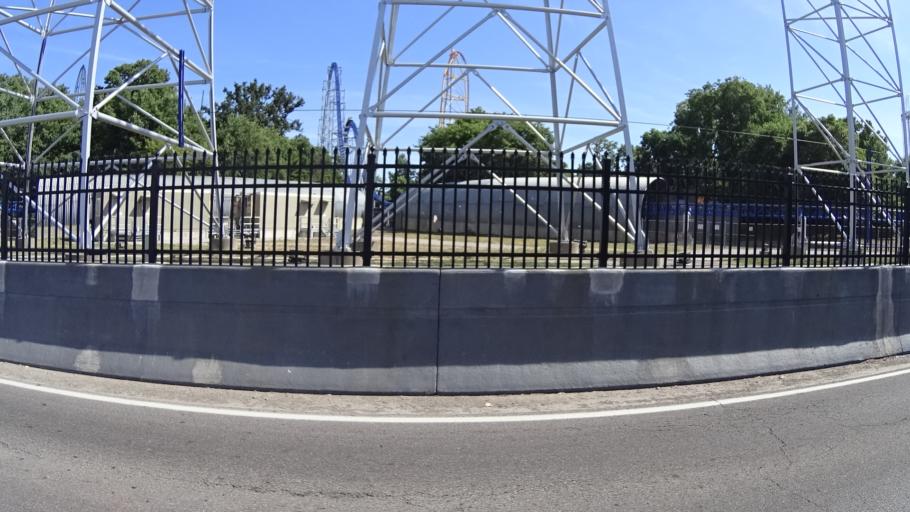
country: US
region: Ohio
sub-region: Erie County
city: Sandusky
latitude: 41.4817
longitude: -82.6892
